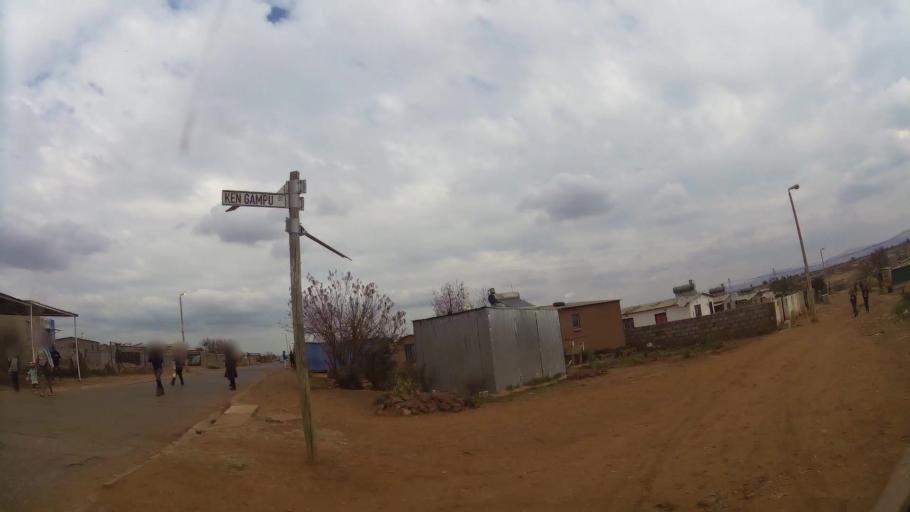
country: ZA
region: Gauteng
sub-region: Ekurhuleni Metropolitan Municipality
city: Germiston
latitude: -26.3789
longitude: 28.1174
